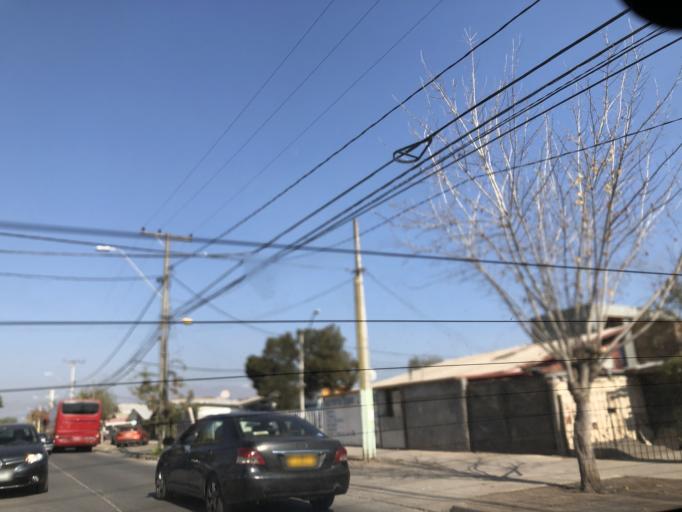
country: CL
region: Santiago Metropolitan
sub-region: Provincia de Cordillera
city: Puente Alto
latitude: -33.6246
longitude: -70.5877
